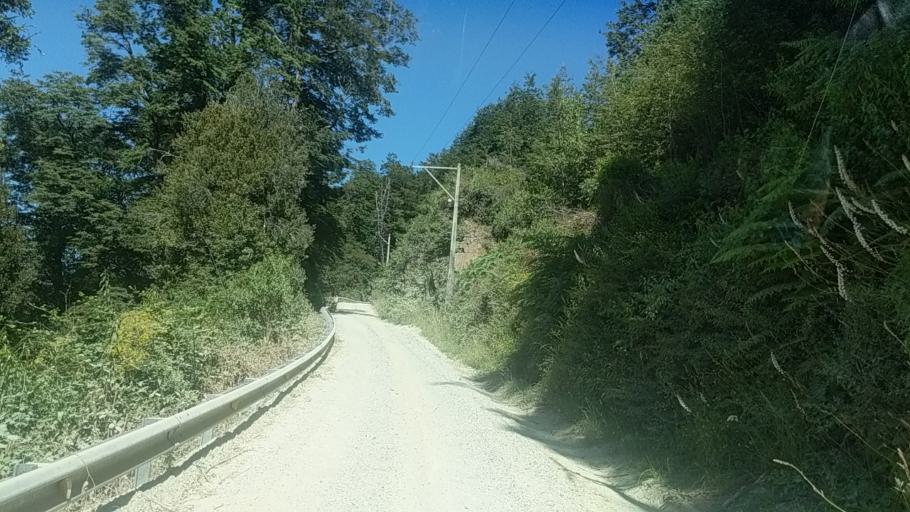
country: CL
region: Araucania
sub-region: Provincia de Cautin
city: Pucon
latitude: -39.0638
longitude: -71.7285
